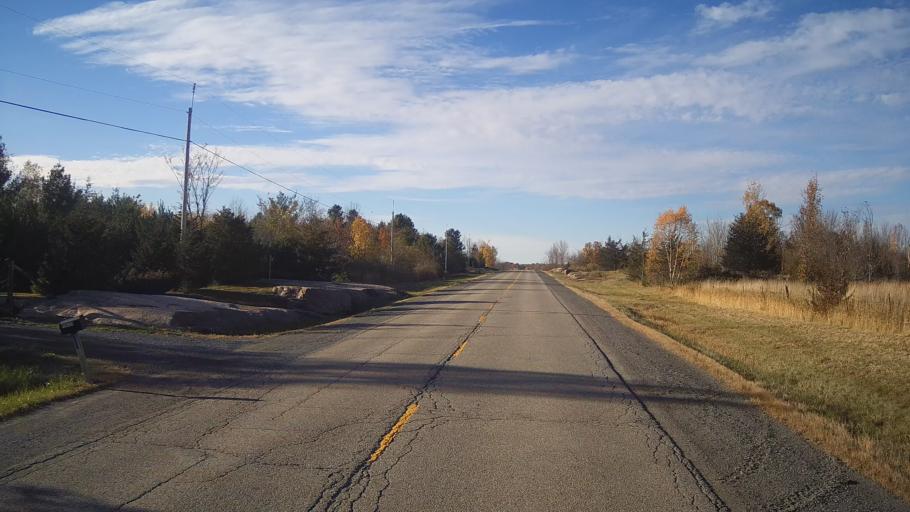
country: CA
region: Ontario
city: Perth
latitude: 44.7113
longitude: -76.4365
